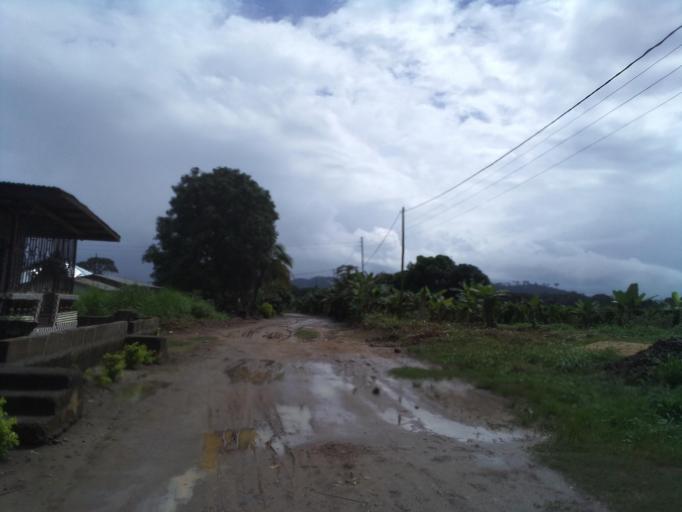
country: SL
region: Eastern Province
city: Kenema
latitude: 7.8494
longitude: -11.1988
